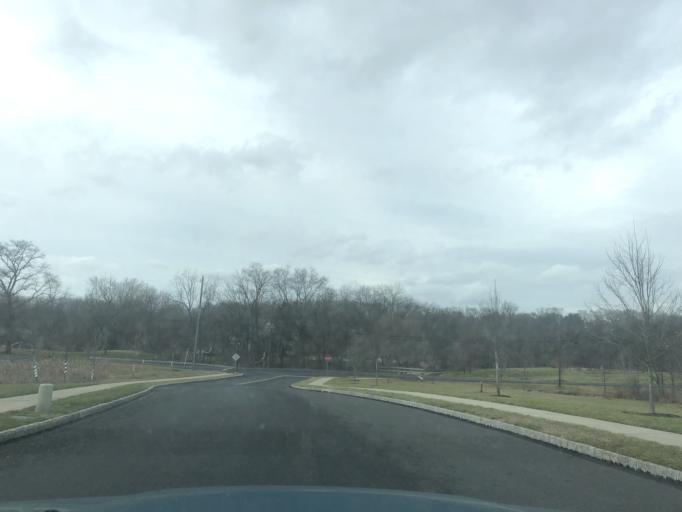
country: US
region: Pennsylvania
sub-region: Montgomery County
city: Harleysville
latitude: 40.2697
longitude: -75.4133
